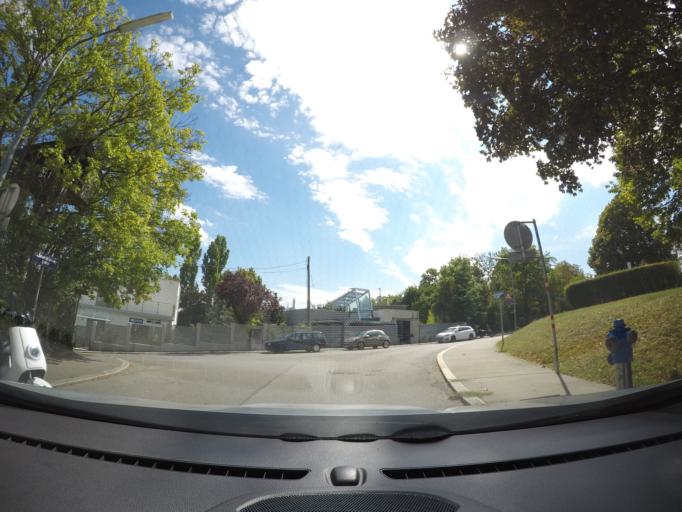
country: AT
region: Lower Austria
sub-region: Politischer Bezirk Modling
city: Perchtoldsdorf
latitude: 48.1785
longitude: 16.2645
